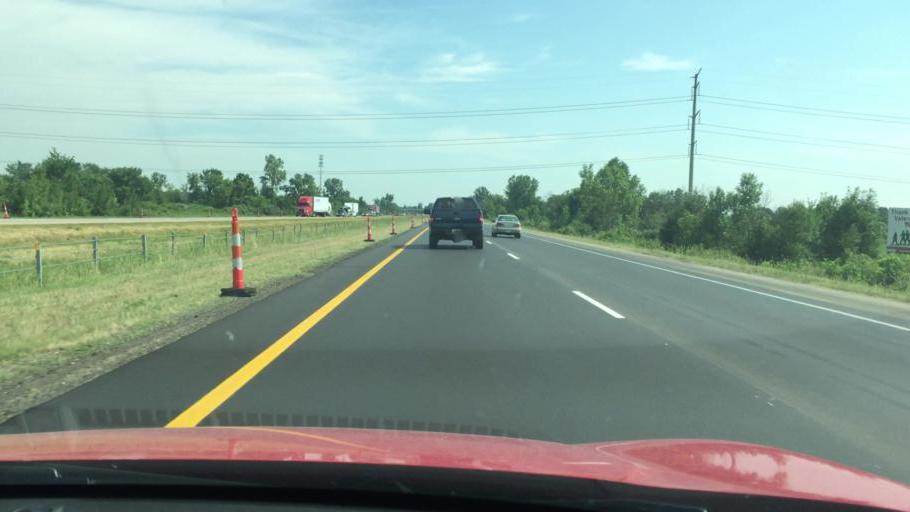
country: US
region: Michigan
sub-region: Washtenaw County
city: Milan
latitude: 42.1227
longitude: -83.6831
